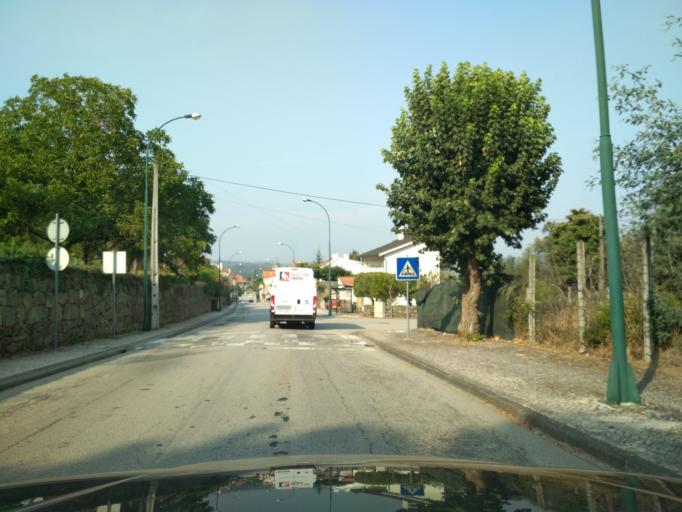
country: PT
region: Viseu
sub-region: Santa Comba Dao
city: Santa Comba Dao
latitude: 40.3930
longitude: -8.1348
